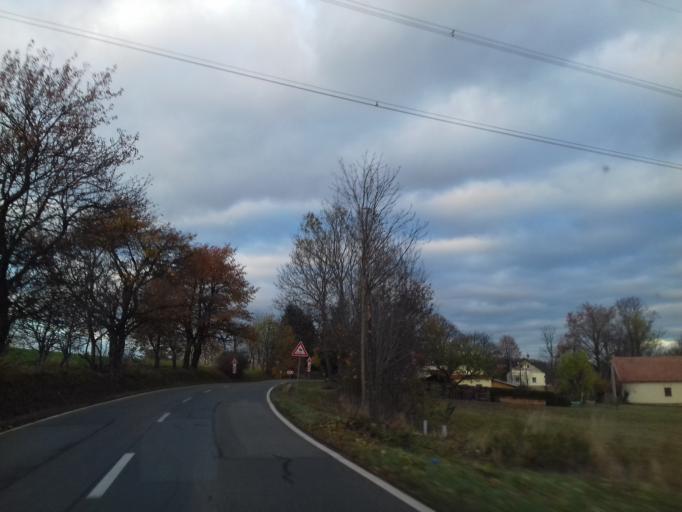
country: CZ
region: Pardubicky
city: Krouna
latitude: 49.7838
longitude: 16.0324
